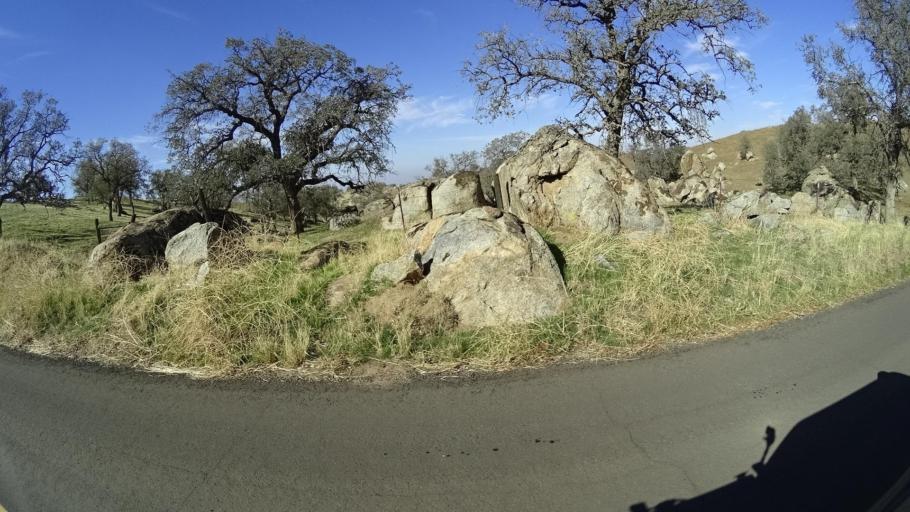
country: US
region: California
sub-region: Kern County
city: Oildale
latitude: 35.6234
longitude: -118.8497
